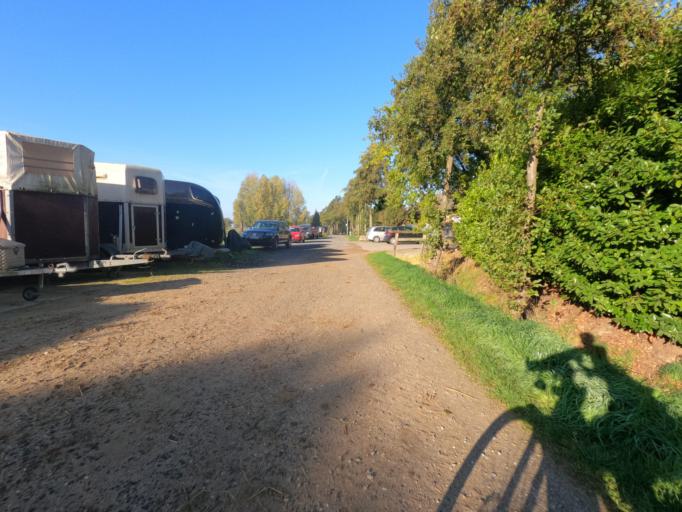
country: DE
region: North Rhine-Westphalia
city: Erkelenz
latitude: 51.0803
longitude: 6.3702
